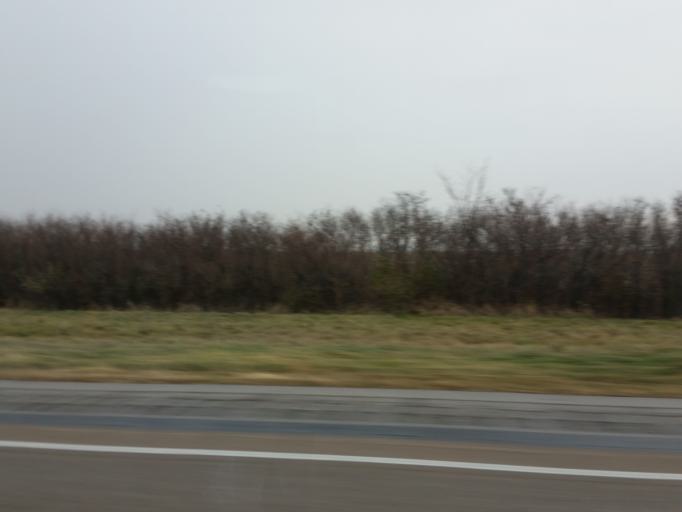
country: US
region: Iowa
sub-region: Cedar County
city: Durant
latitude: 41.6331
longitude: -90.8856
